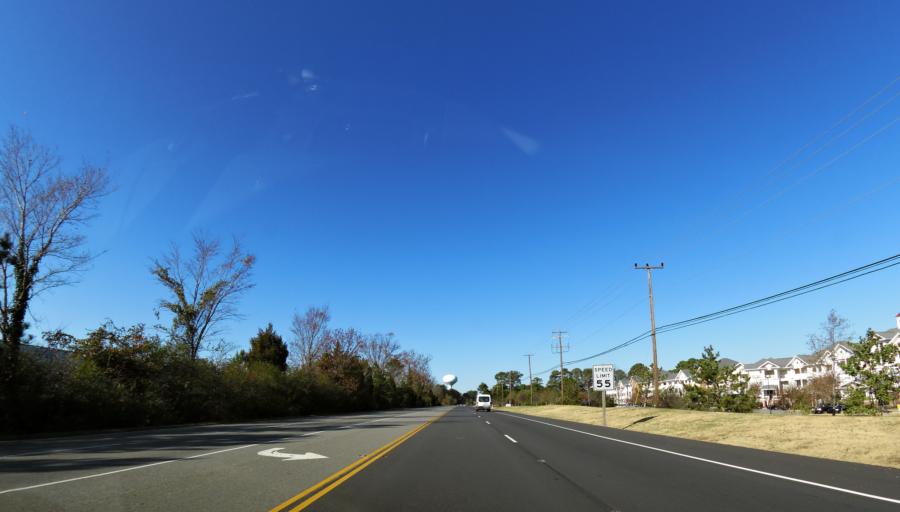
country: US
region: Virginia
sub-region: City of Williamsburg
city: Williamsburg
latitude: 37.2386
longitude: -76.6404
